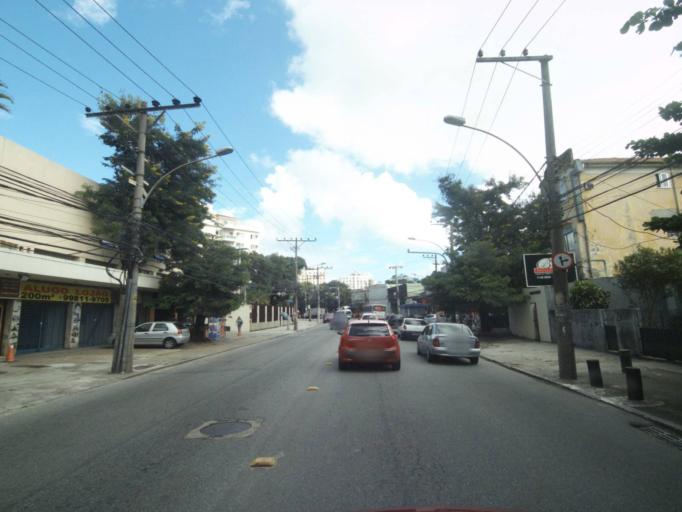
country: BR
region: Rio de Janeiro
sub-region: Sao Joao De Meriti
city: Sao Joao de Meriti
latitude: -22.9230
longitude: -43.3610
